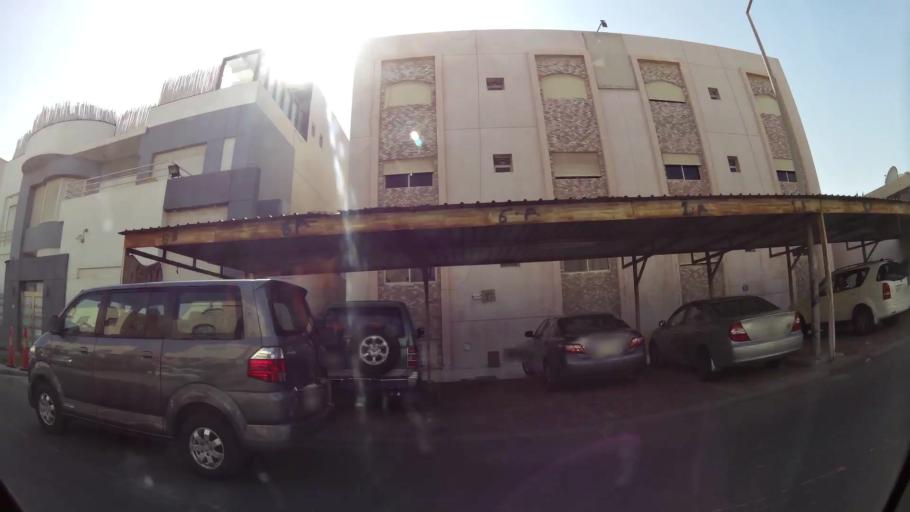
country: KW
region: Muhafazat Hawalli
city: Salwa
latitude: 29.2848
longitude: 48.0767
